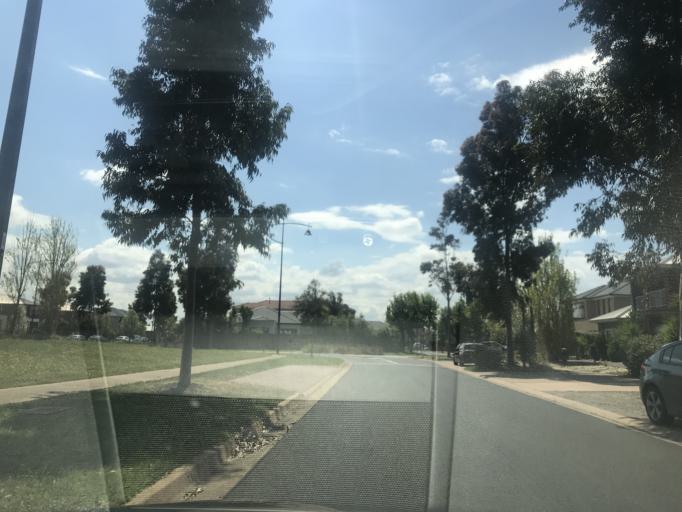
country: AU
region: Victoria
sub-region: Wyndham
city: Williams Landing
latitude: -37.8858
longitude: 144.7299
